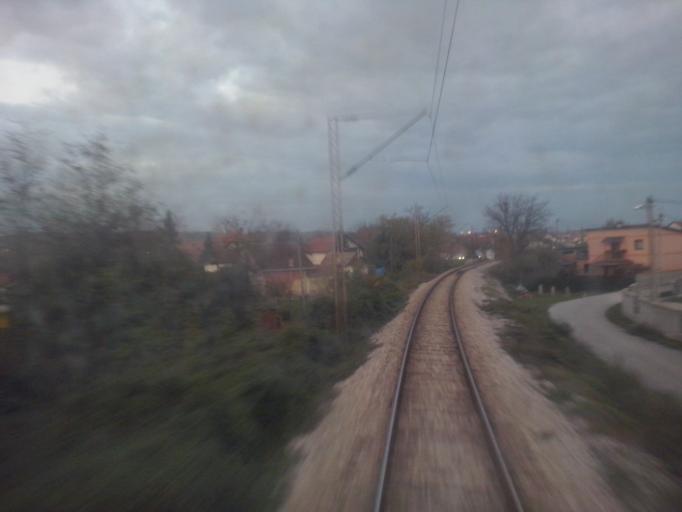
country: RS
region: Central Serbia
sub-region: Kolubarski Okrug
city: Valjevo
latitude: 44.2782
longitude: 19.9250
